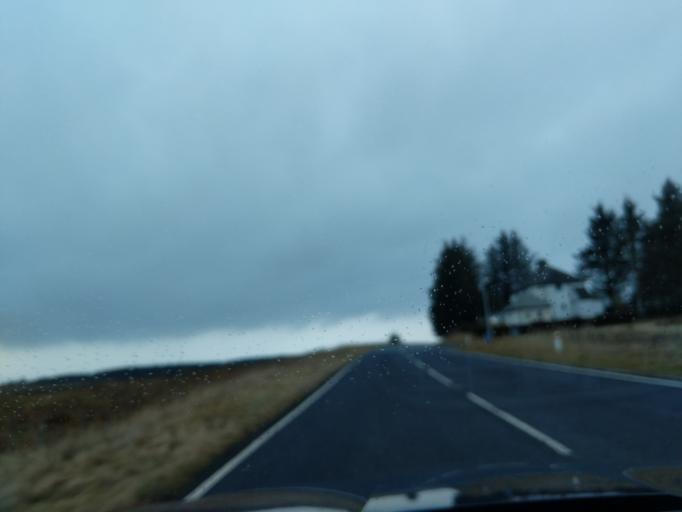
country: GB
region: England
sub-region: Northumberland
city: Corsenside
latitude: 55.1977
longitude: -2.0869
